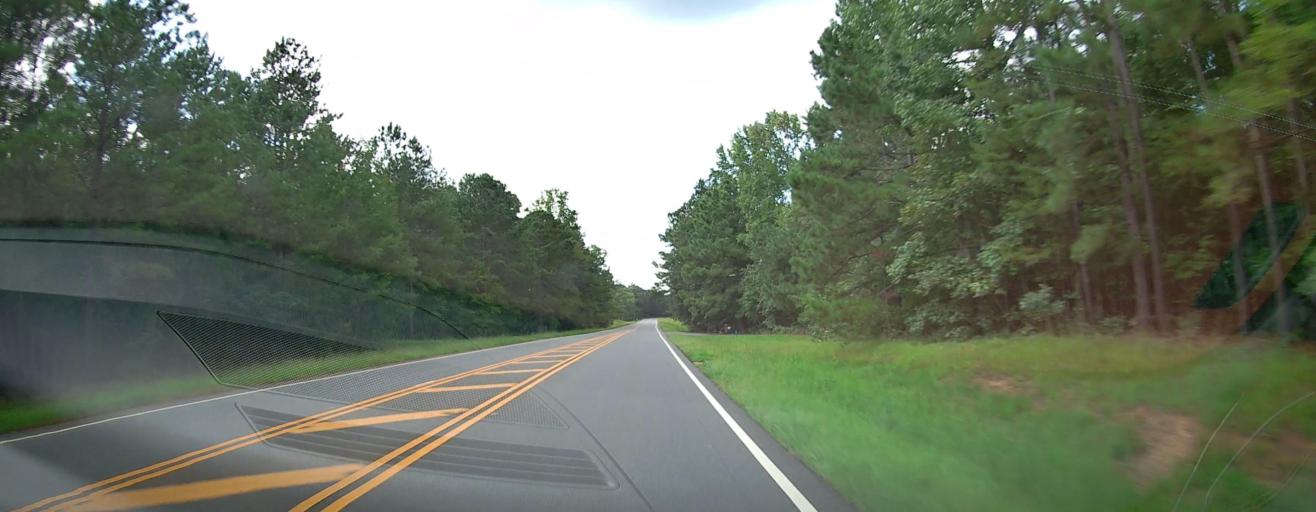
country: US
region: Georgia
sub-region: Bibb County
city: West Point
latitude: 32.8747
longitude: -83.9222
